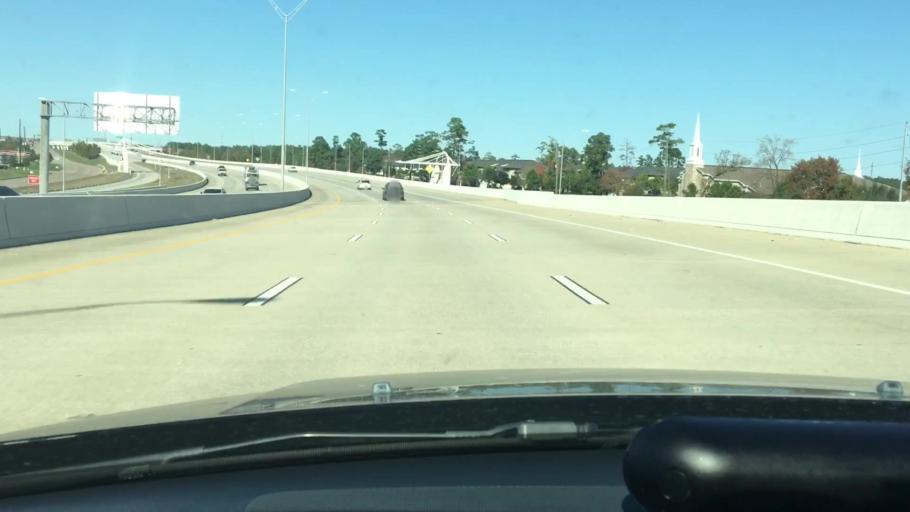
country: US
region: Texas
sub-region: Harris County
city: Atascocita
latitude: 29.9265
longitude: -95.2005
